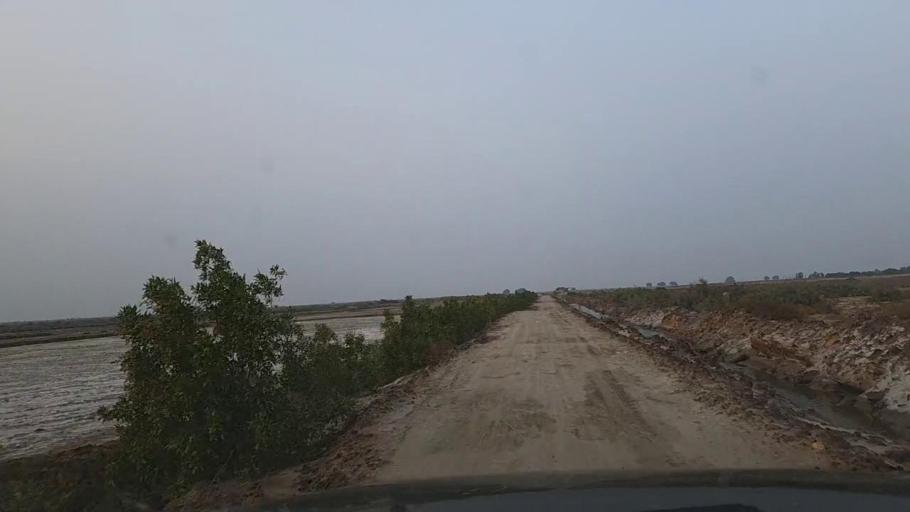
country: PK
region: Sindh
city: Gharo
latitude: 24.7439
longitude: 67.7204
